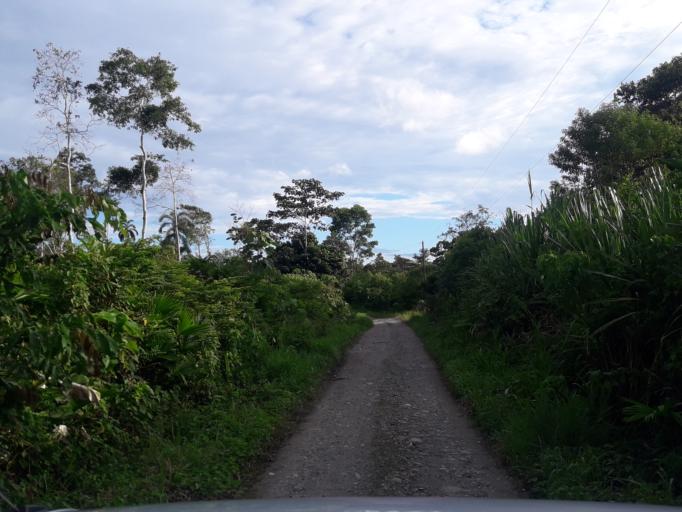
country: EC
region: Orellana
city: Boca Suno
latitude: -0.9015
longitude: -77.3108
